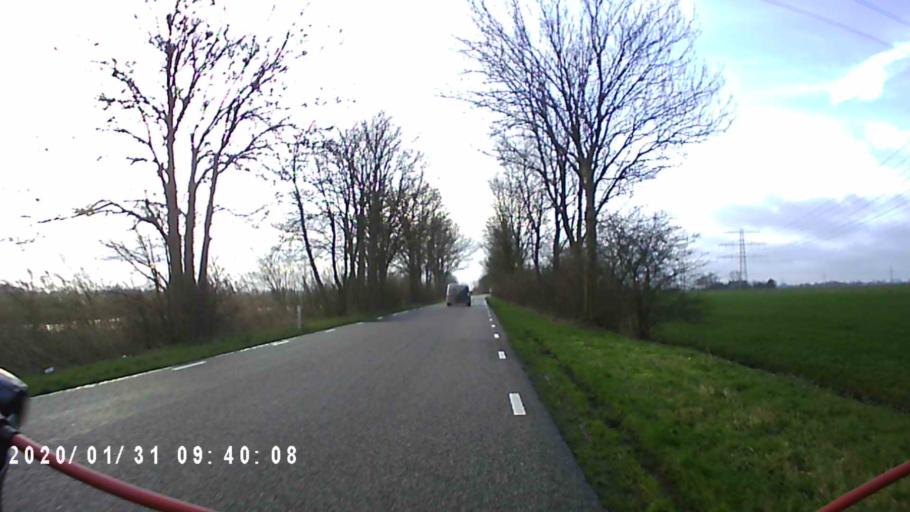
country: NL
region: Groningen
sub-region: Gemeente Zuidhorn
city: Aduard
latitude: 53.2866
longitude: 6.4840
